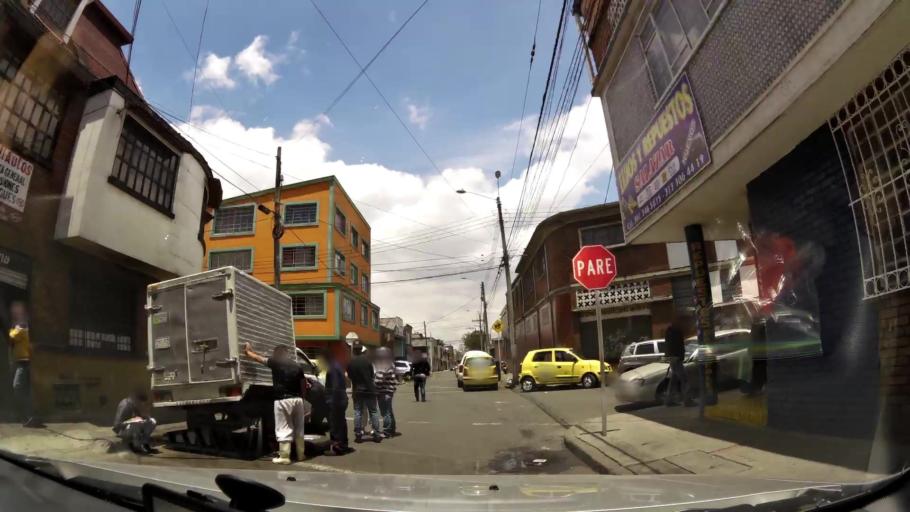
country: CO
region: Bogota D.C.
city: Bogota
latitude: 4.5936
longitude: -74.0921
